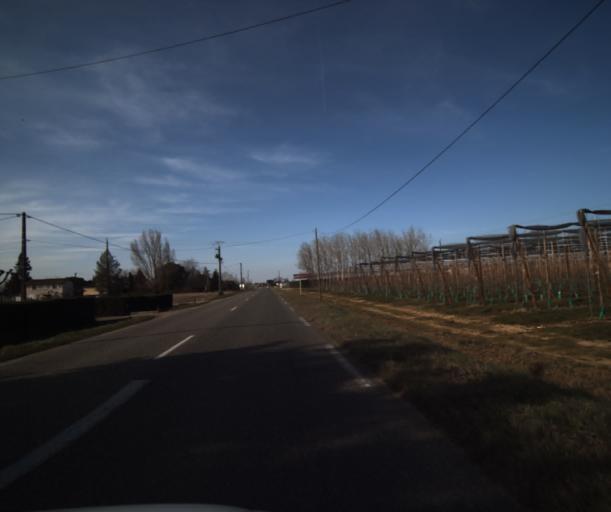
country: FR
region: Midi-Pyrenees
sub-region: Departement du Tarn-et-Garonne
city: Corbarieu
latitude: 43.9372
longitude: 1.3586
